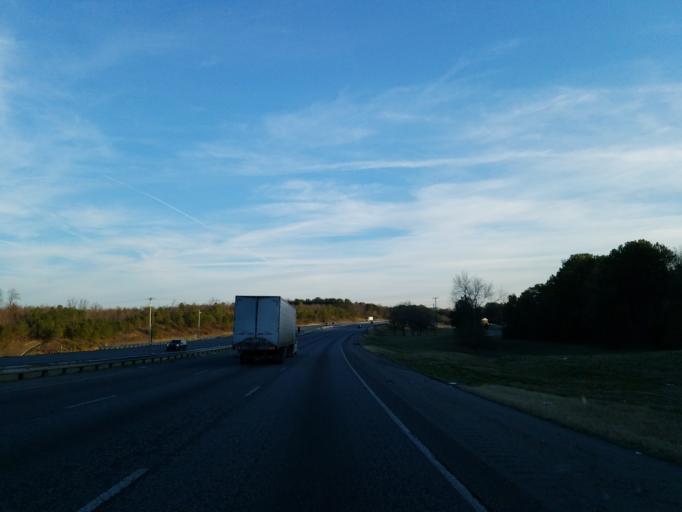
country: US
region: Georgia
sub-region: Gordon County
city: Calhoun
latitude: 34.5429
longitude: -84.9228
